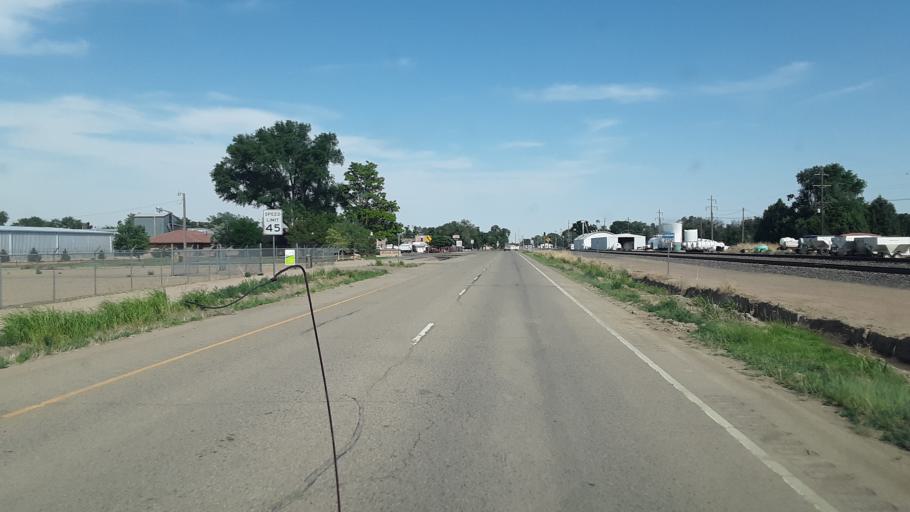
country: US
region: Colorado
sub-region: Otero County
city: Rocky Ford
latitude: 38.0584
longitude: -103.7335
